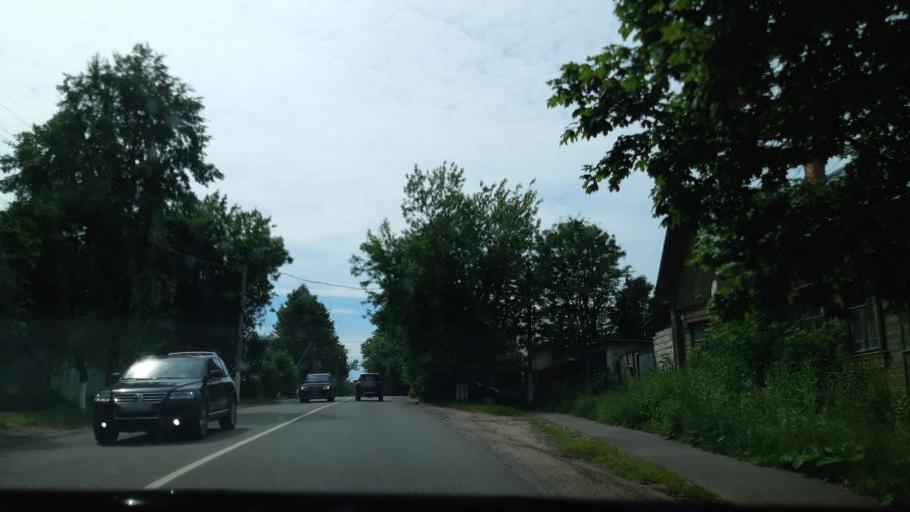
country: RU
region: Moskovskaya
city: Vereya
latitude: 55.3428
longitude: 36.1921
